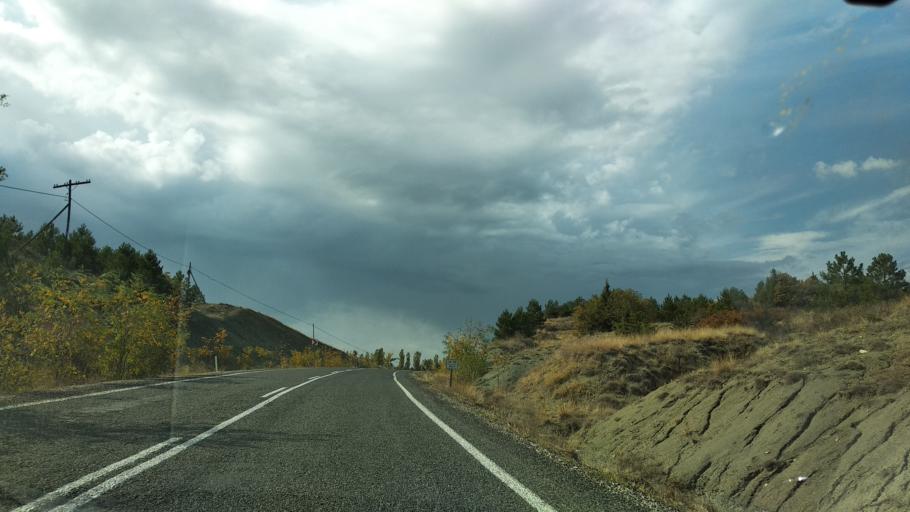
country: TR
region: Bolu
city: Seben
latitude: 40.3852
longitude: 31.5357
